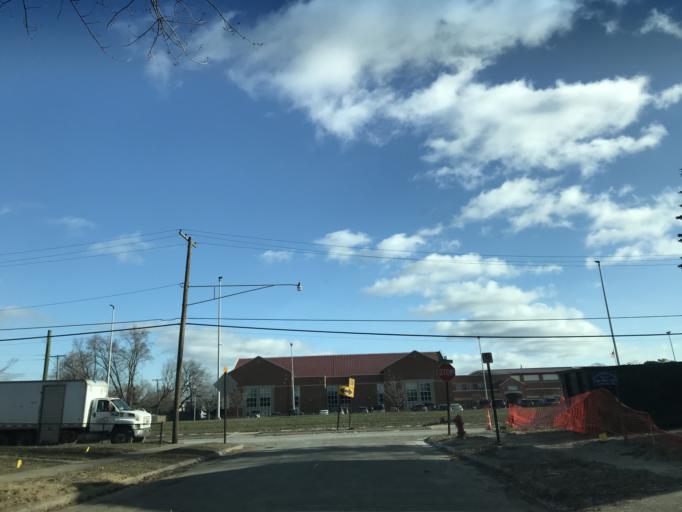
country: US
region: Michigan
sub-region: Oakland County
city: Hazel Park
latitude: 42.4599
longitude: -83.1012
